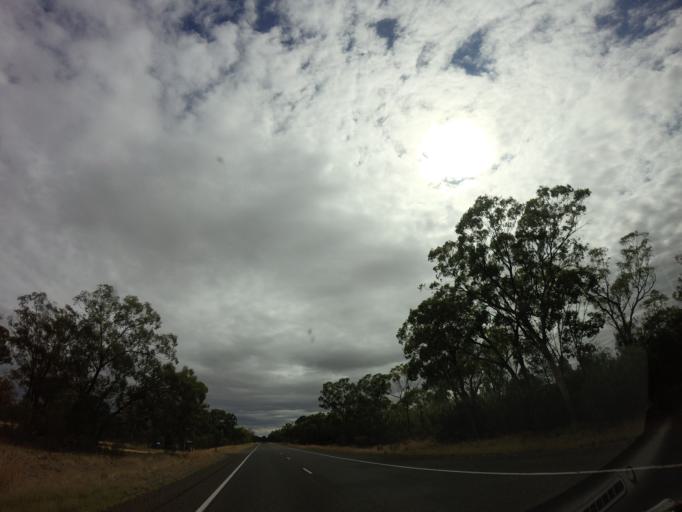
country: AU
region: New South Wales
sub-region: Narrabri
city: Narrabri
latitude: -30.3723
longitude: 149.7294
